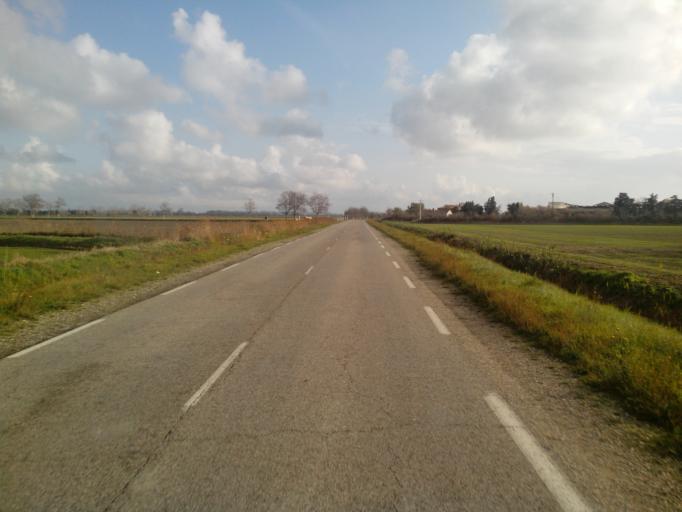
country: FR
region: Provence-Alpes-Cote d'Azur
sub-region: Departement des Bouches-du-Rhone
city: Port-Saint-Louis-du-Rhone
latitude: 43.4652
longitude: 4.7130
